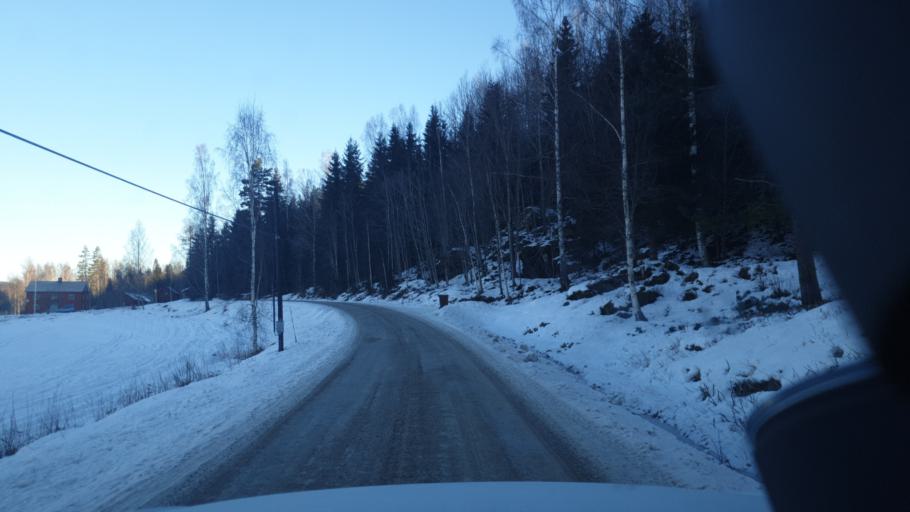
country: SE
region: Vaermland
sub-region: Arvika Kommun
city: Arvika
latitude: 59.7321
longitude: 12.8331
